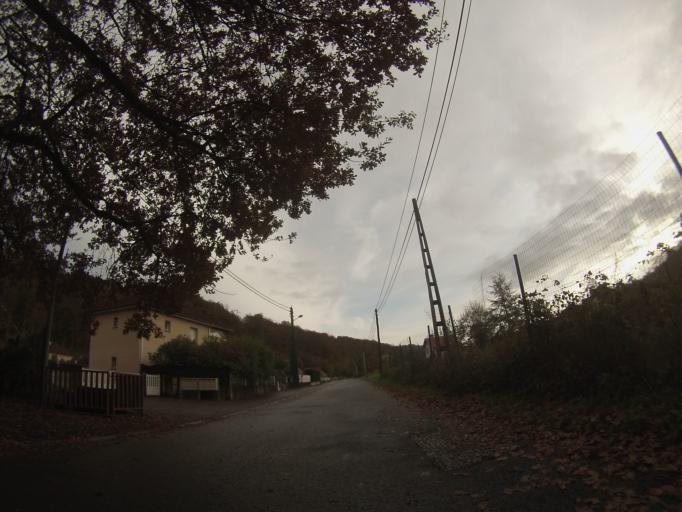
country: FR
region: Aquitaine
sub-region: Departement des Pyrenees-Atlantiques
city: Jurancon
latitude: 43.2756
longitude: -0.3863
